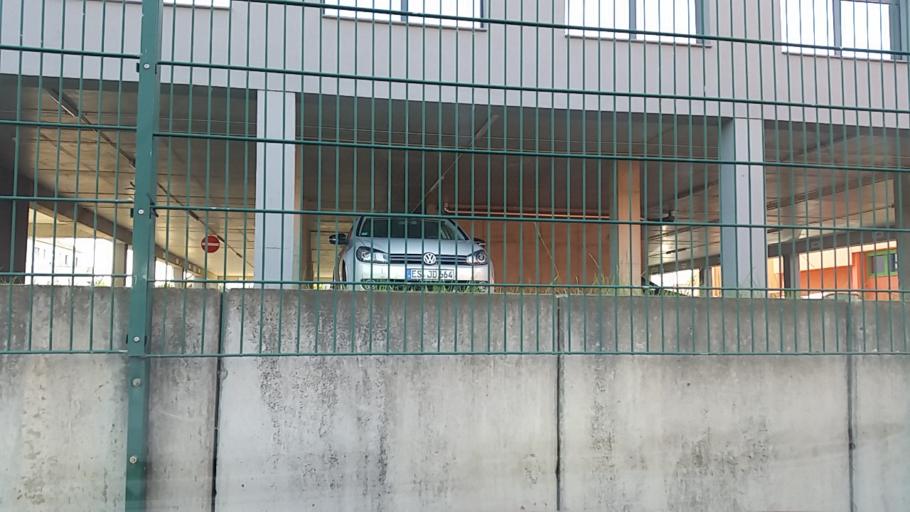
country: DE
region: Lower Saxony
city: Weyhausen
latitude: 52.4224
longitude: 10.7244
